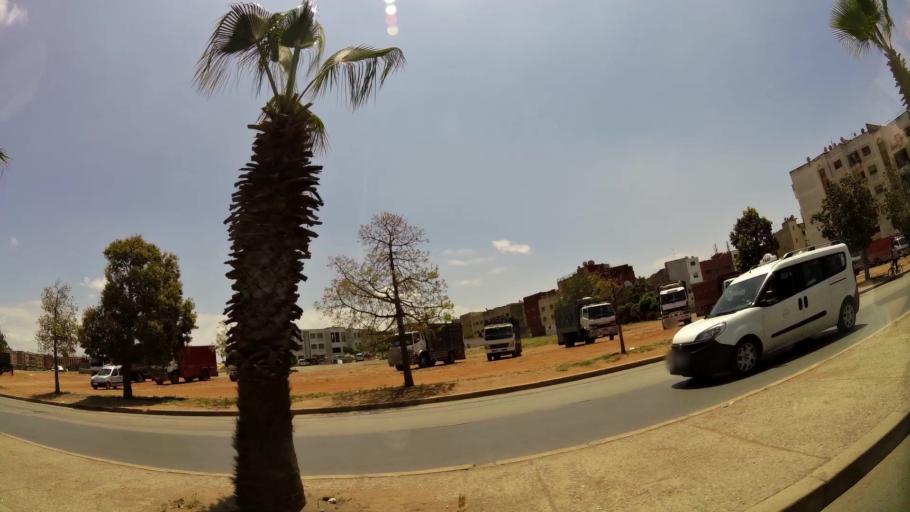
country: MA
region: Rabat-Sale-Zemmour-Zaer
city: Sale
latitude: 34.0562
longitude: -6.7915
